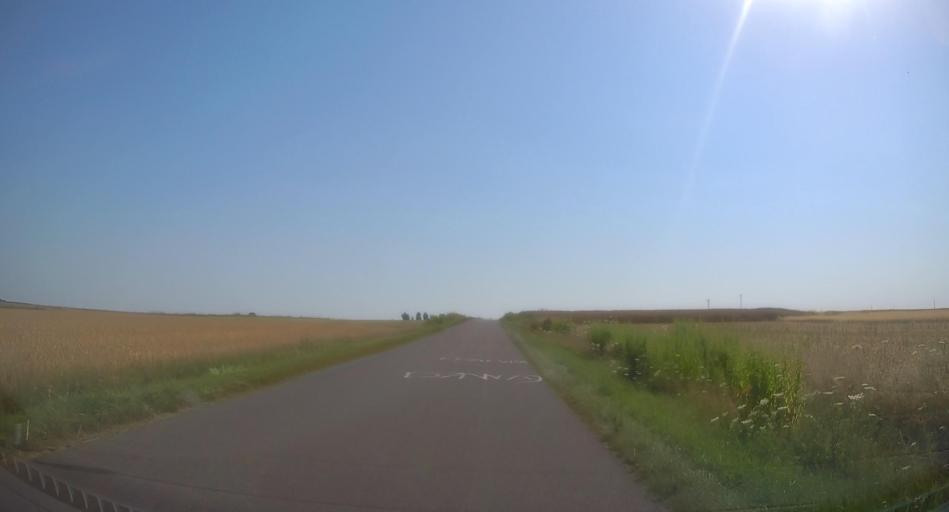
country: PL
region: Lodz Voivodeship
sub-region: Powiat skierniewicki
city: Kaweczyn Nowy
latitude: 51.8857
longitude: 20.2234
